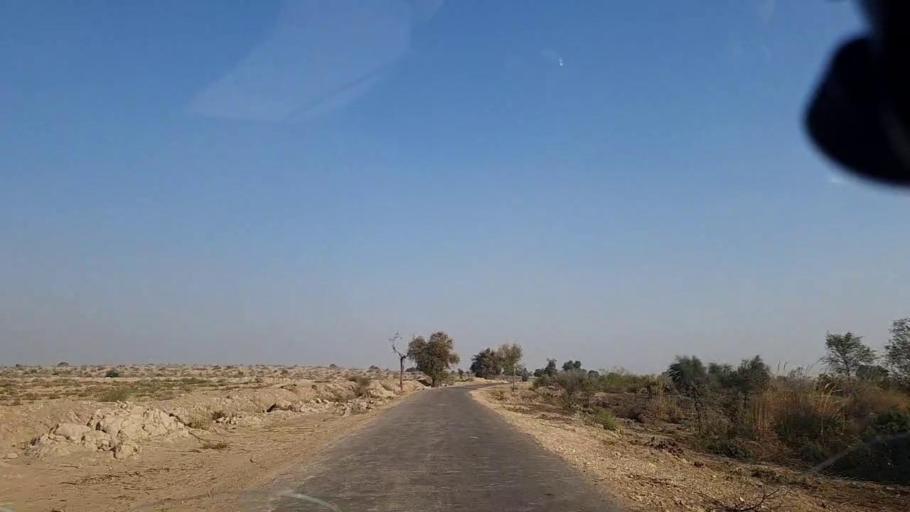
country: PK
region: Sindh
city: Khanpur
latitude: 27.6819
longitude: 69.5521
